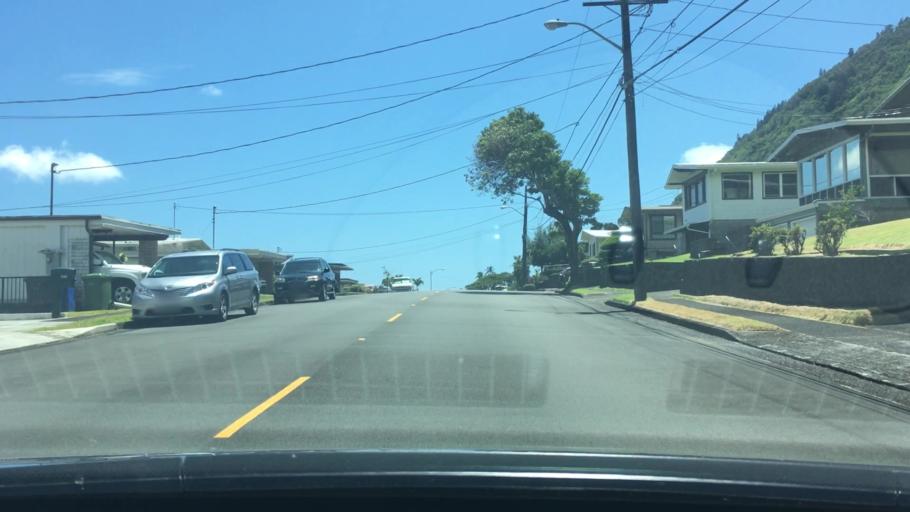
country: US
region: Hawaii
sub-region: Honolulu County
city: Honolulu
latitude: 21.3228
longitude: -157.8059
